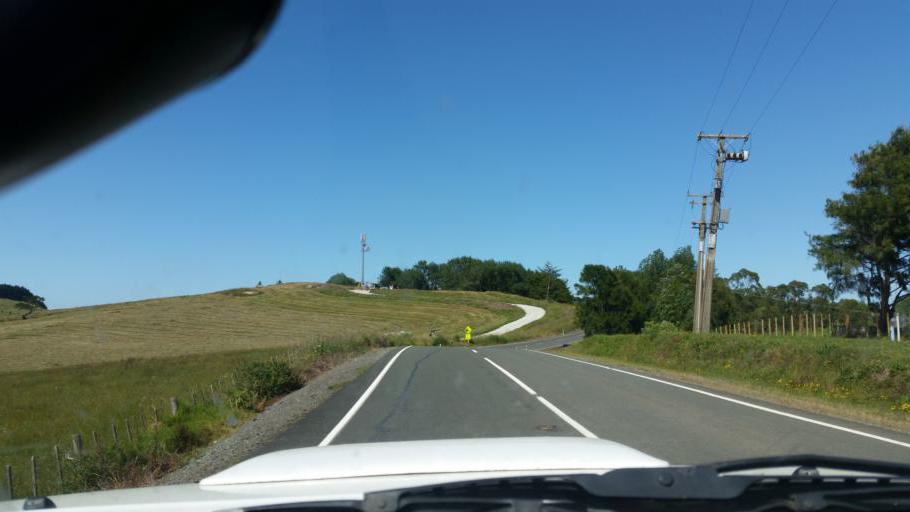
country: NZ
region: Auckland
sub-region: Auckland
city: Wellsford
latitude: -36.2243
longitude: 174.3751
